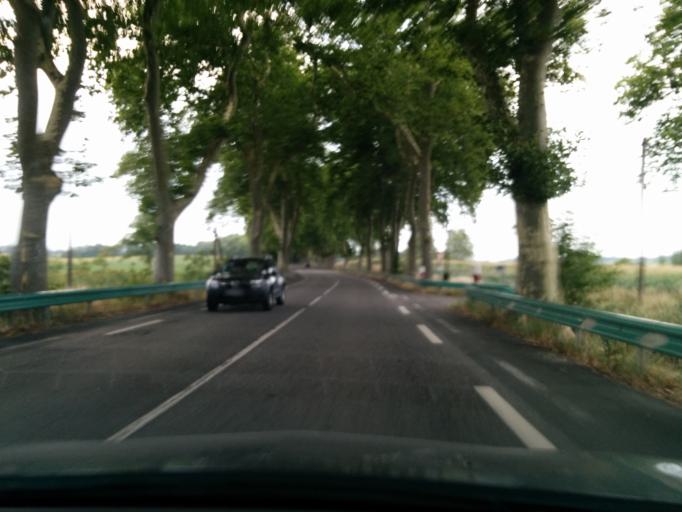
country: FR
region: Midi-Pyrenees
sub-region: Departement de la Haute-Garonne
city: Villefranche-de-Lauragais
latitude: 43.4120
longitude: 1.7037
